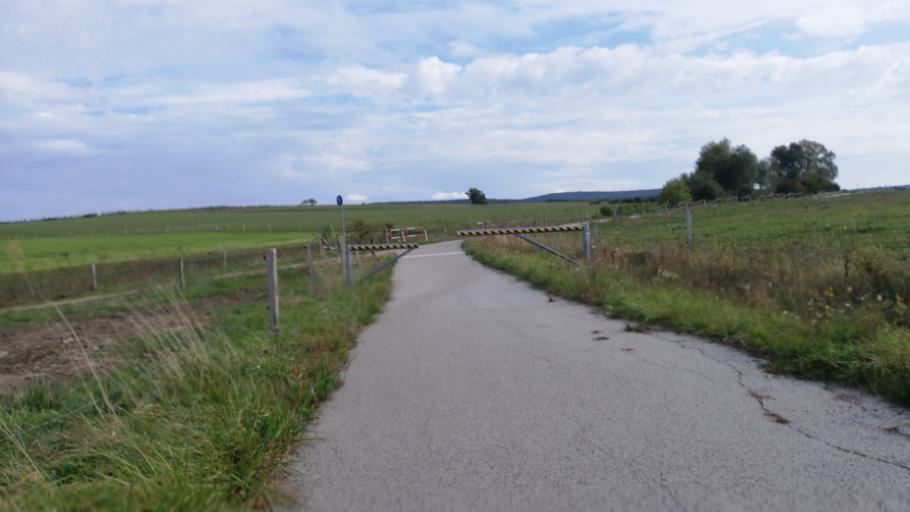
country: CZ
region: South Moravian
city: Sudomerice
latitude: 48.8422
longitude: 17.2816
